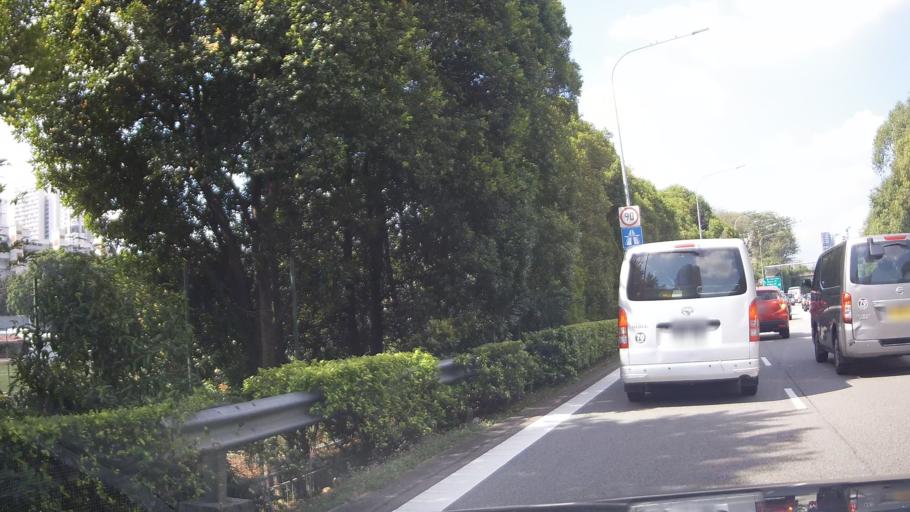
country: SG
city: Singapore
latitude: 1.3265
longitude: 103.8614
